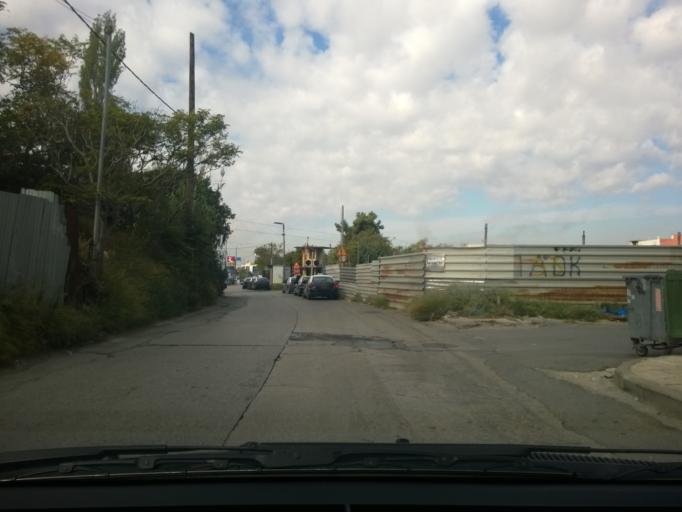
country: GR
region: Central Macedonia
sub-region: Nomos Thessalonikis
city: Menemeni
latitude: 40.6530
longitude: 22.9072
